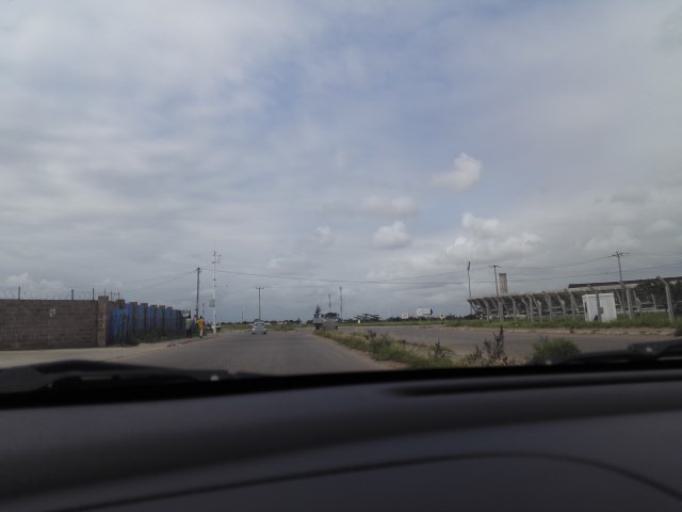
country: MZ
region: Maputo City
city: Maputo
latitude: -25.8255
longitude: 32.5800
